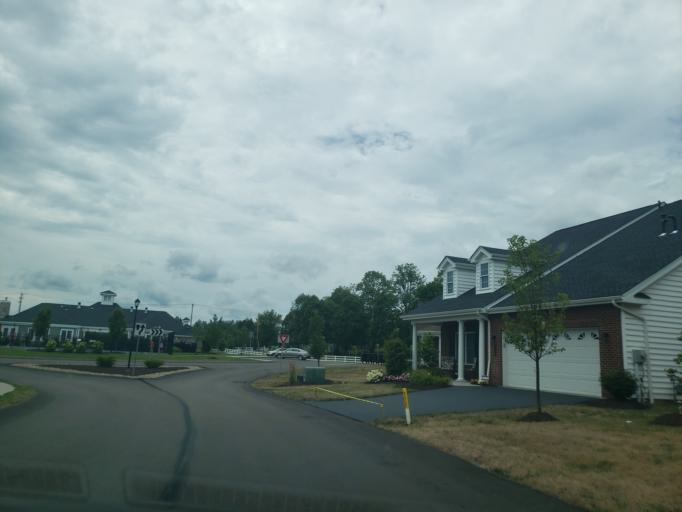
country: US
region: Pennsylvania
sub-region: Allegheny County
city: Emsworth
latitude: 40.5372
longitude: -80.0942
